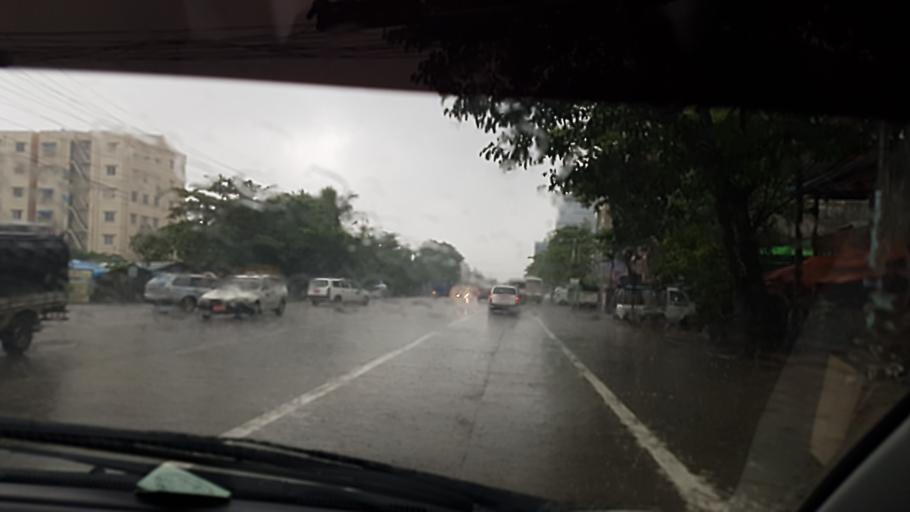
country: MM
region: Yangon
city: Yangon
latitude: 16.7807
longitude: 96.1896
